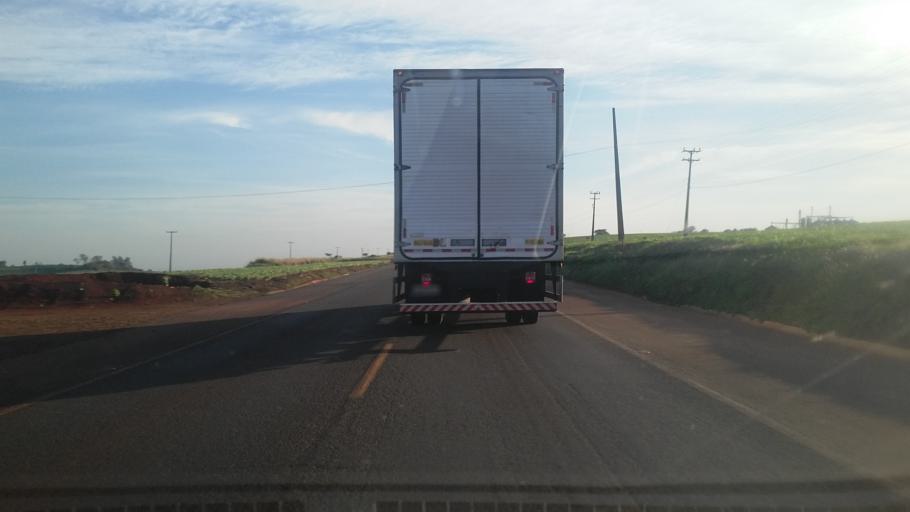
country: BR
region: Parana
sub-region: Bandeirantes
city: Bandeirantes
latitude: -23.1479
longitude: -50.5945
